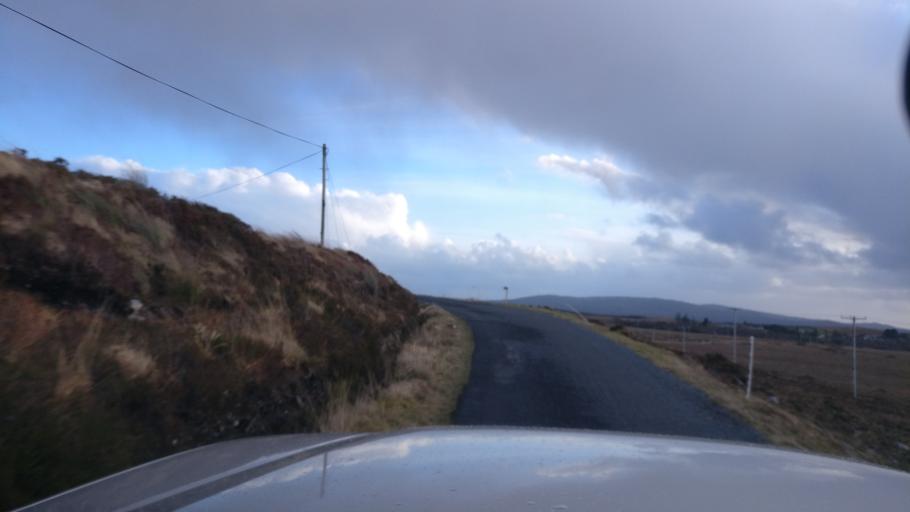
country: IE
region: Connaught
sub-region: County Galway
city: Clifden
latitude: 53.4739
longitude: -9.6924
